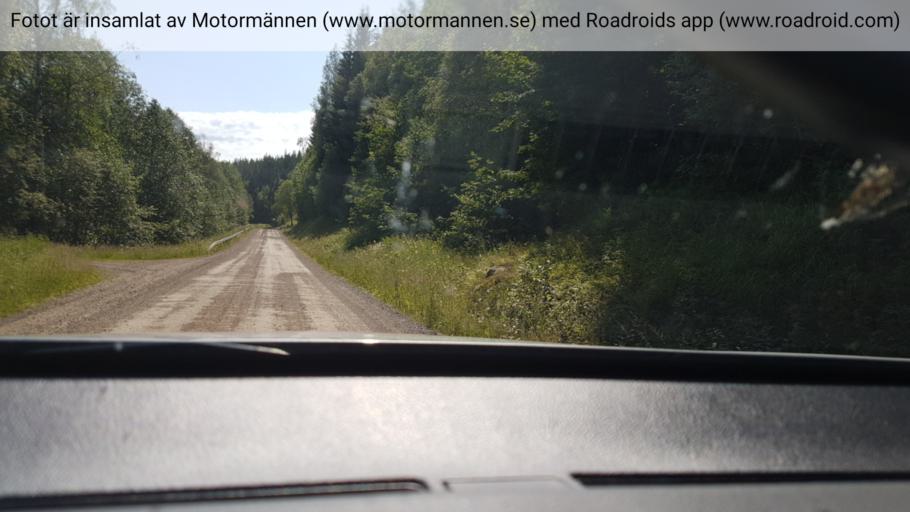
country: SE
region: Vaermland
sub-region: Torsby Kommun
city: Torsby
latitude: 60.4345
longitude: 13.2304
